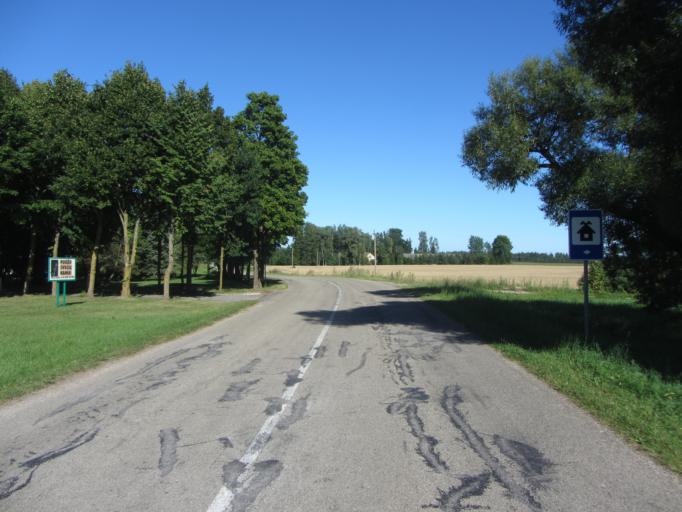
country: LT
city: Obeliai
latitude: 55.8091
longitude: 25.1637
